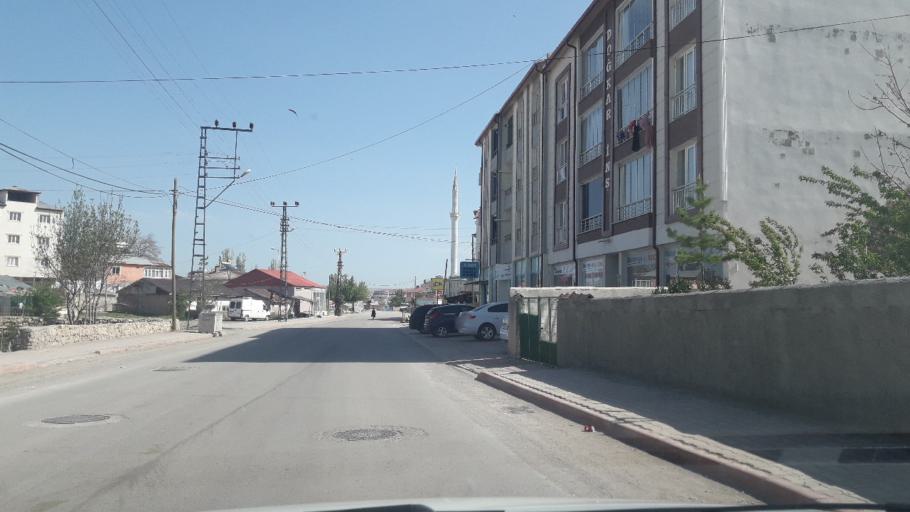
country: TR
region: Sivas
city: Kangal
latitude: 39.2306
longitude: 37.3886
